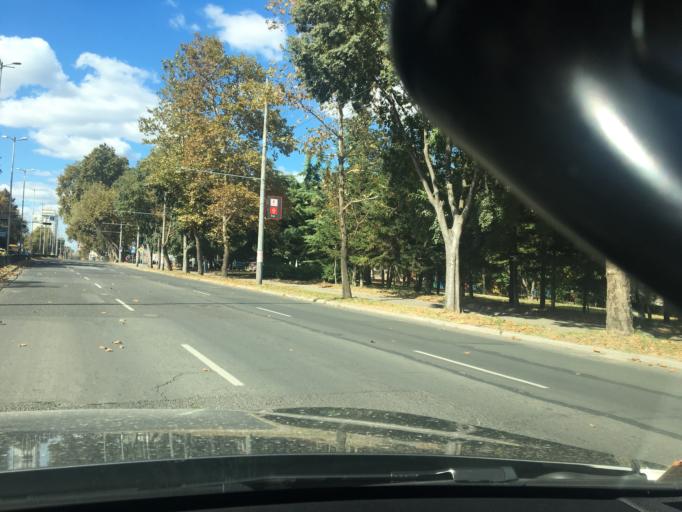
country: BG
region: Burgas
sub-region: Obshtina Burgas
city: Burgas
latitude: 42.5050
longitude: 27.4735
